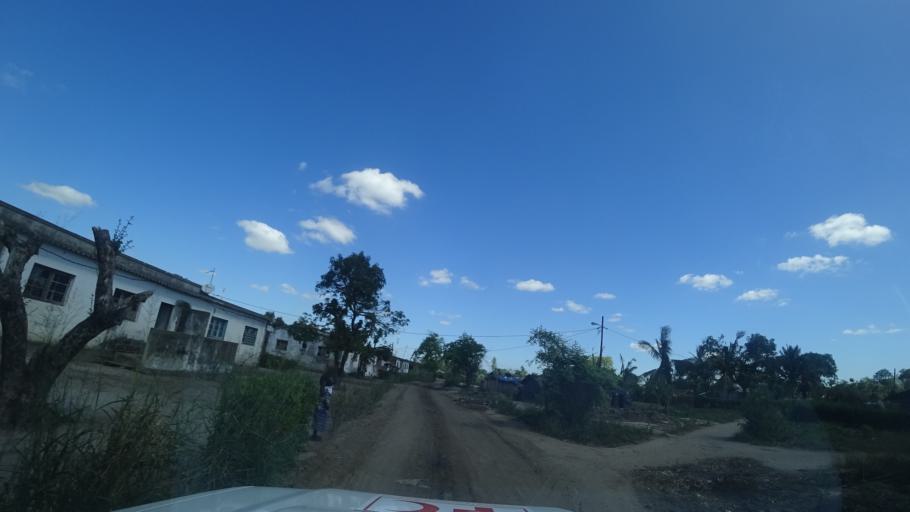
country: MZ
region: Sofala
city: Dondo
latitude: -19.4967
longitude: 34.5964
